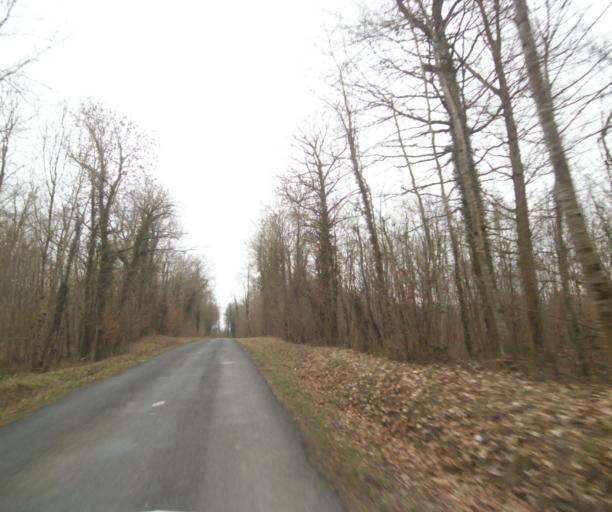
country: FR
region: Champagne-Ardenne
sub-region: Departement de la Haute-Marne
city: Bienville
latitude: 48.5683
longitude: 5.0185
